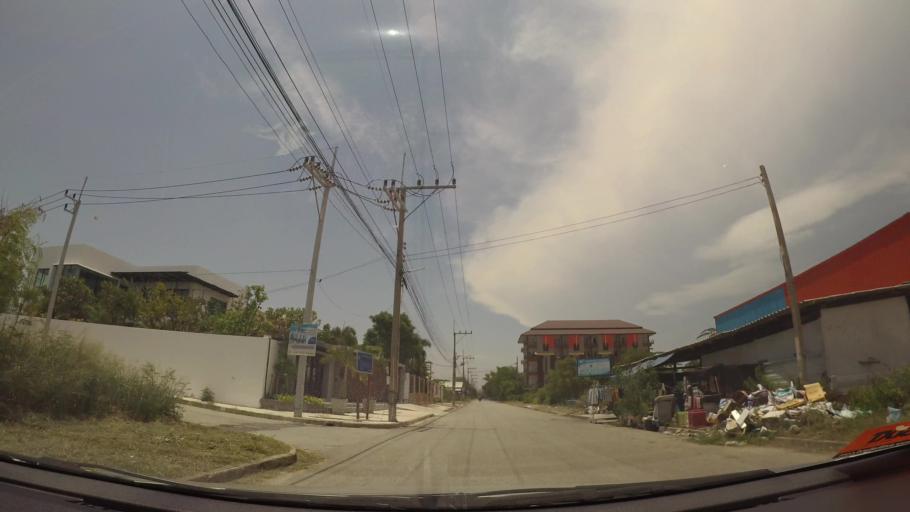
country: TH
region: Chon Buri
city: Chon Buri
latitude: 13.3391
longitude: 100.9523
